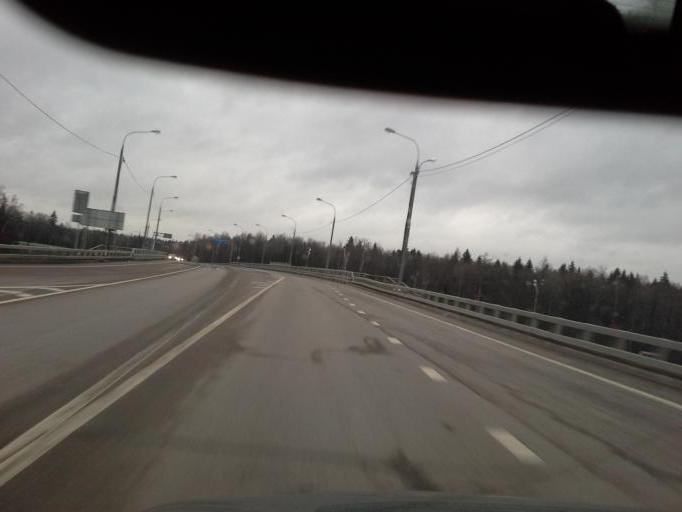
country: RU
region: Moskovskaya
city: Kokoshkino
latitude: 55.6225
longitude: 37.1547
